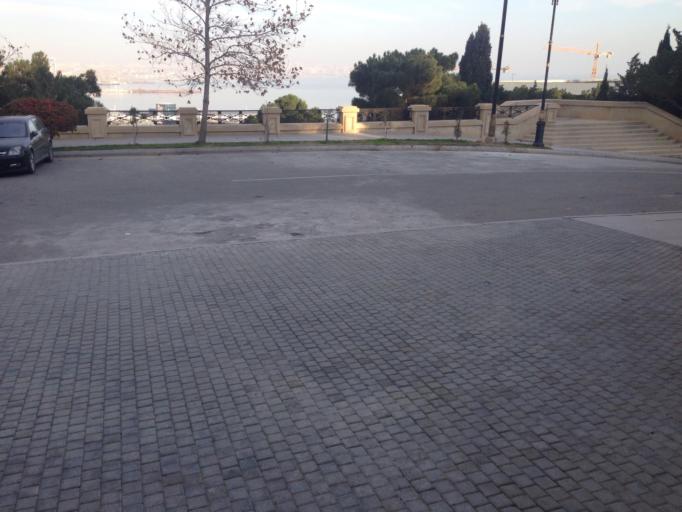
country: AZ
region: Baki
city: Badamdar
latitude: 40.3593
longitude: 49.8301
